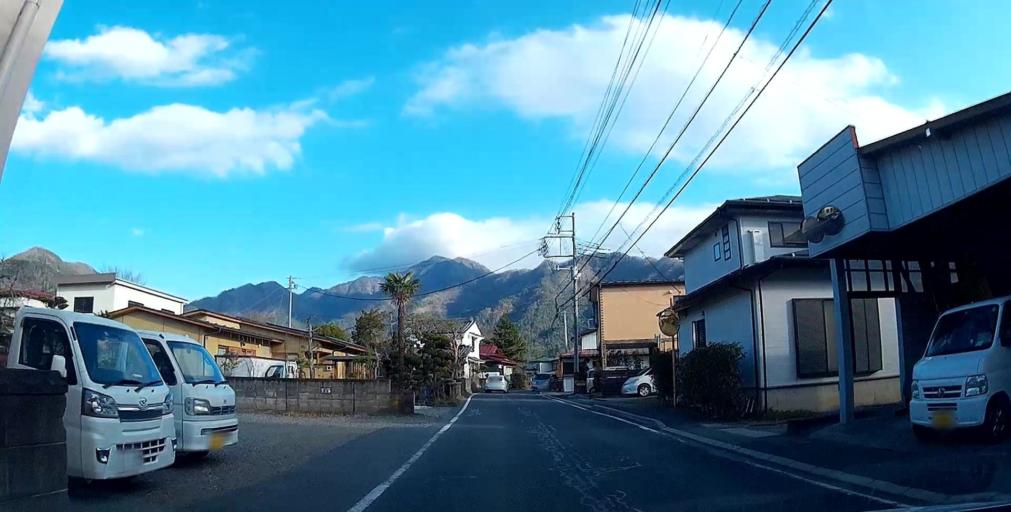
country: JP
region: Yamanashi
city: Fujikawaguchiko
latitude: 35.4941
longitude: 138.8247
